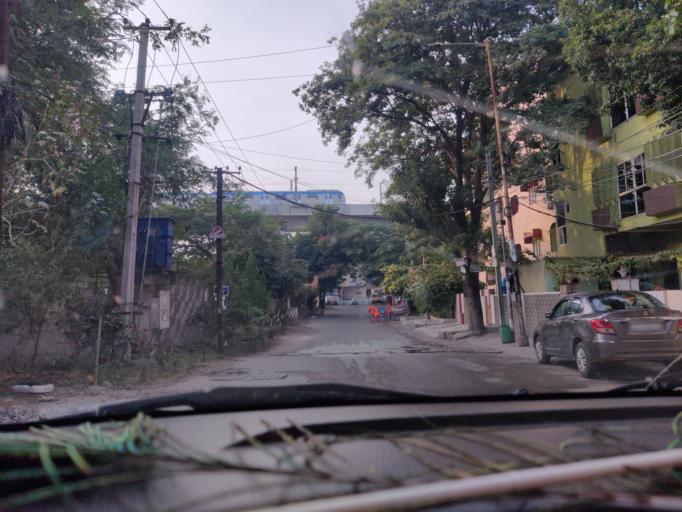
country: IN
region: Telangana
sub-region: Rangareddi
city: Kukatpalli
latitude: 17.4385
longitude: 78.4404
